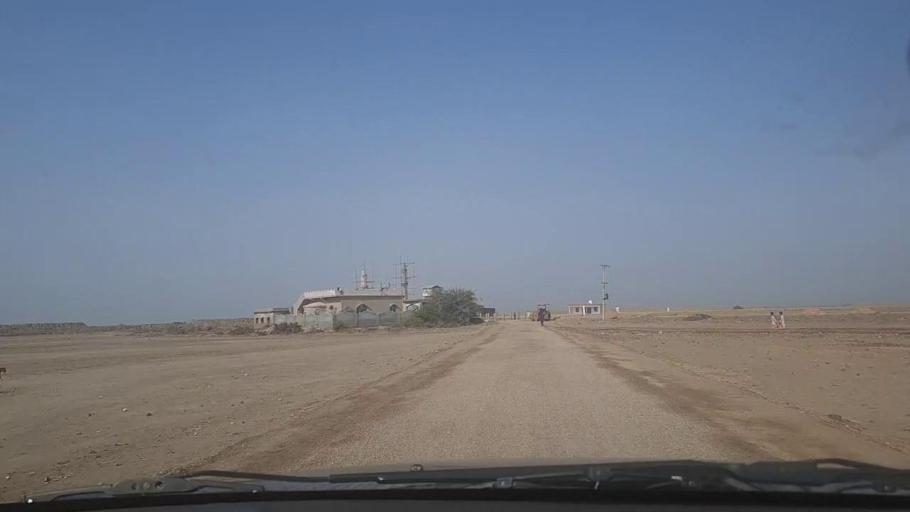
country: PK
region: Sindh
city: Keti Bandar
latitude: 24.1824
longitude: 67.5027
